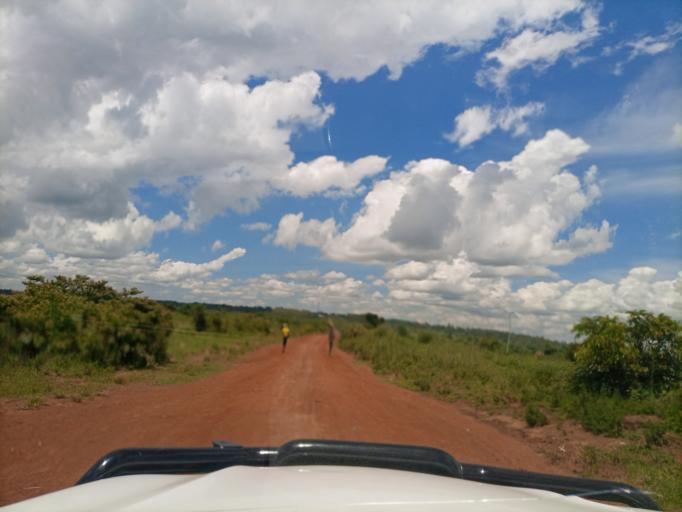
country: UG
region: Eastern Region
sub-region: Busia District
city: Busia
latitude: 0.6276
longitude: 33.9903
